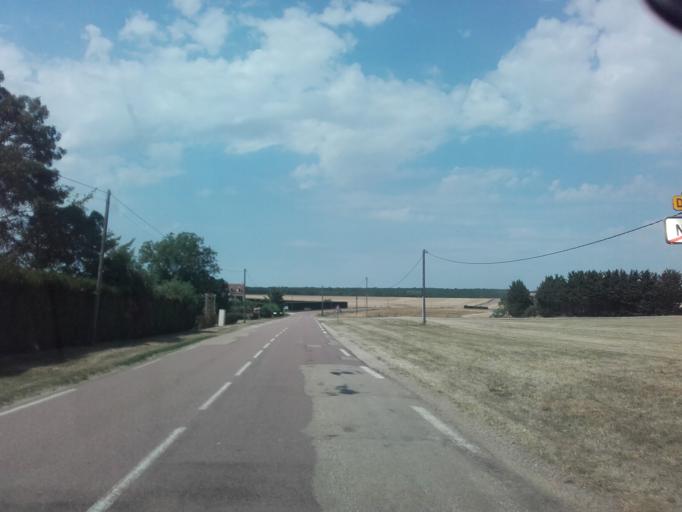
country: FR
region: Bourgogne
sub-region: Departement de l'Yonne
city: Joux-la-Ville
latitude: 47.6752
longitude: 3.8761
